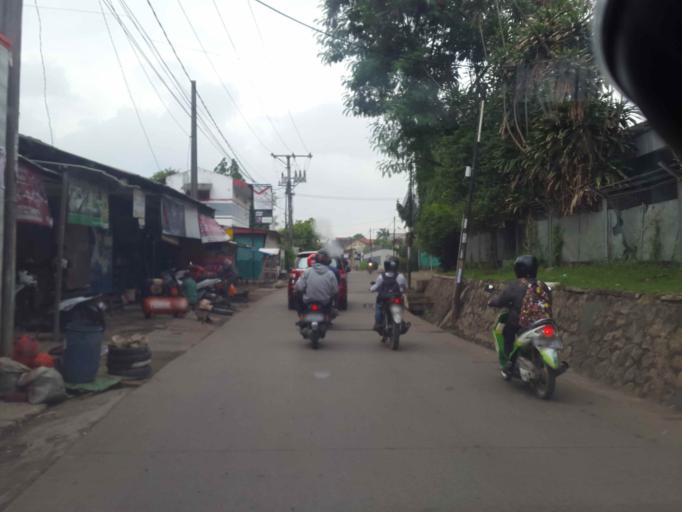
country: ID
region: West Java
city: Bekasi
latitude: -6.2514
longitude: 107.0416
